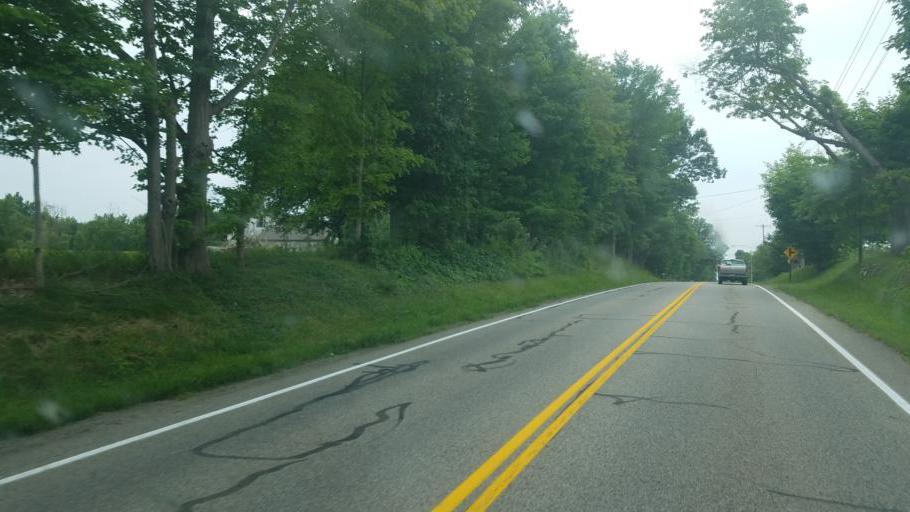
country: US
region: Ohio
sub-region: Portage County
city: Brimfield
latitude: 41.1000
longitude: -81.2850
